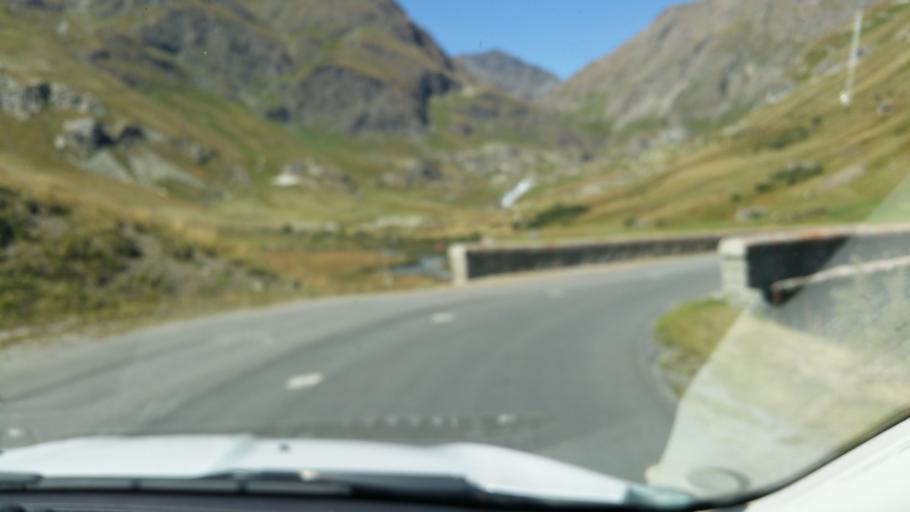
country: FR
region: Rhone-Alpes
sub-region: Departement de la Savoie
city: Val-d'Isere
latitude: 45.3847
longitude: 7.0425
